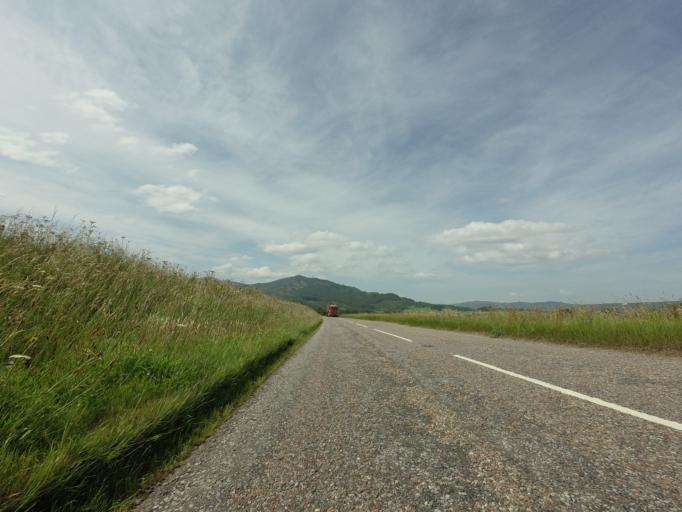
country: GB
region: Scotland
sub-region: Highland
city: Tain
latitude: 57.8394
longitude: -4.1892
